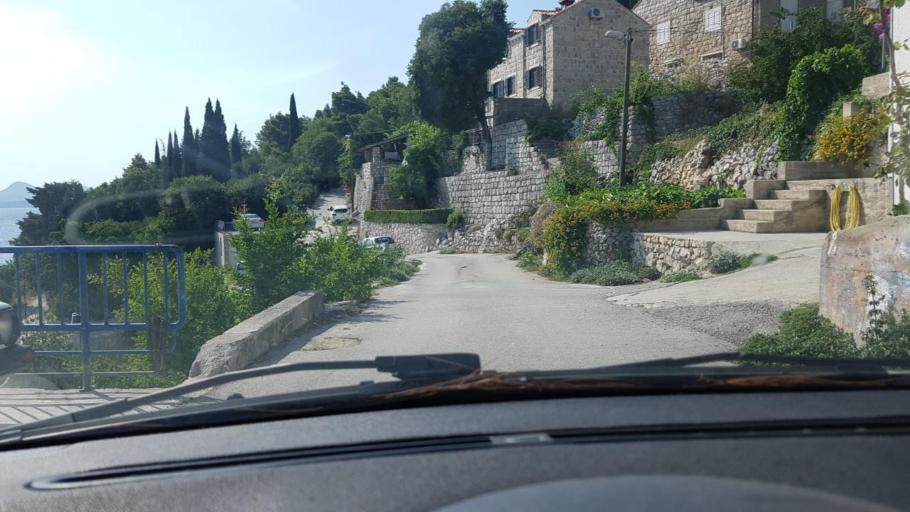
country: HR
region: Dubrovacko-Neretvanska
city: Podgora
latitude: 42.7844
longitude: 17.8611
